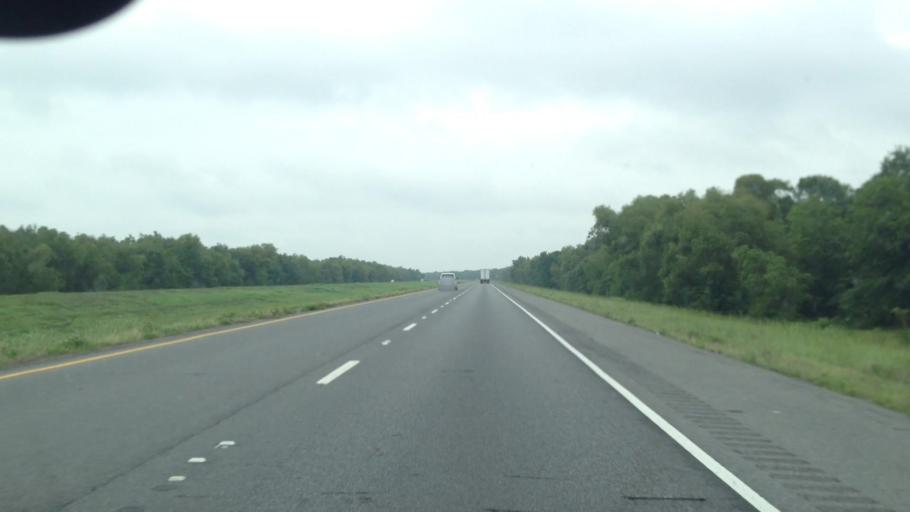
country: US
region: Louisiana
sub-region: Saint Landry Parish
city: Opelousas
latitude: 30.6783
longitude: -92.0749
